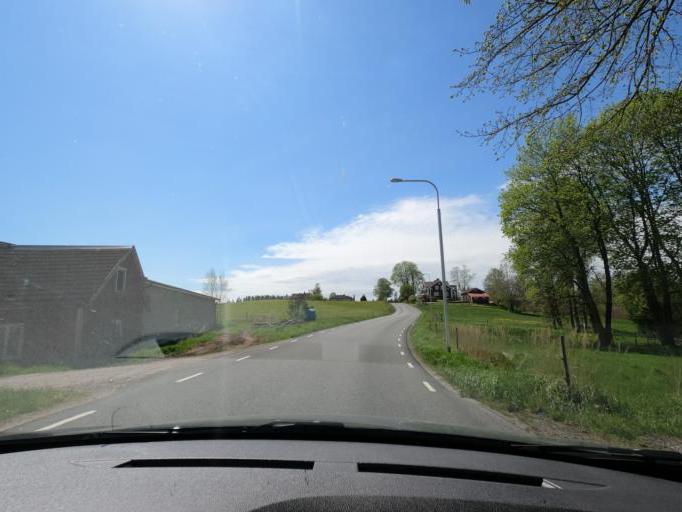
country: SE
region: Joenkoeping
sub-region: Varnamo Kommun
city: Bredaryd
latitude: 57.1655
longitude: 13.7391
